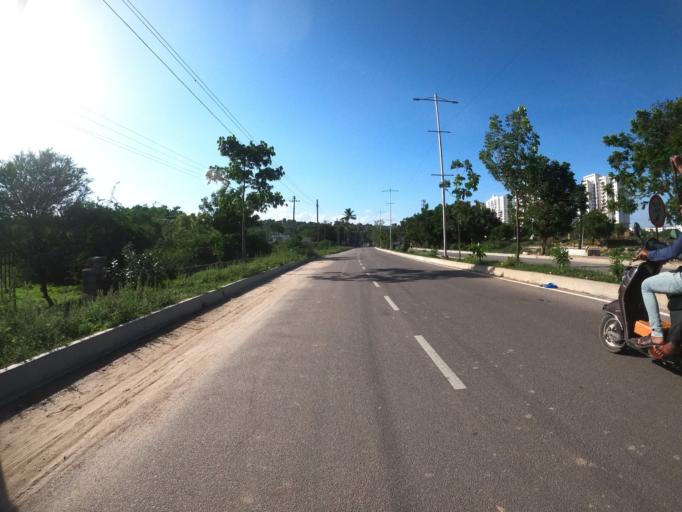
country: IN
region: Telangana
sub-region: Hyderabad
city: Hyderabad
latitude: 17.3558
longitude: 78.3697
